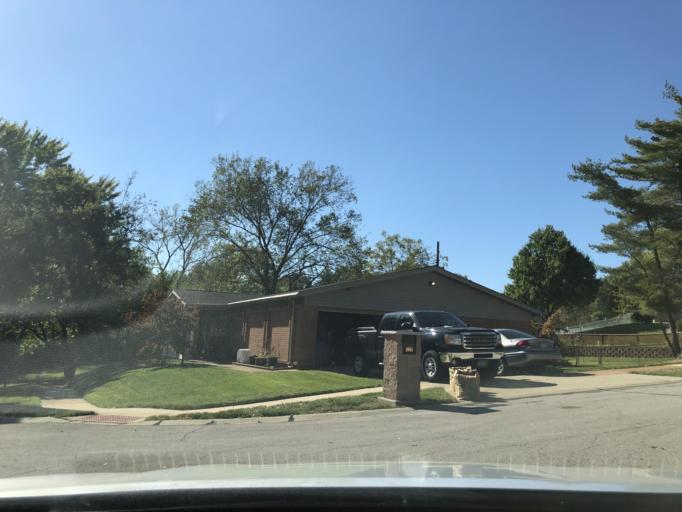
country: US
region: Missouri
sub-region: Saint Louis County
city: Concord
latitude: 38.4938
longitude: -90.3651
